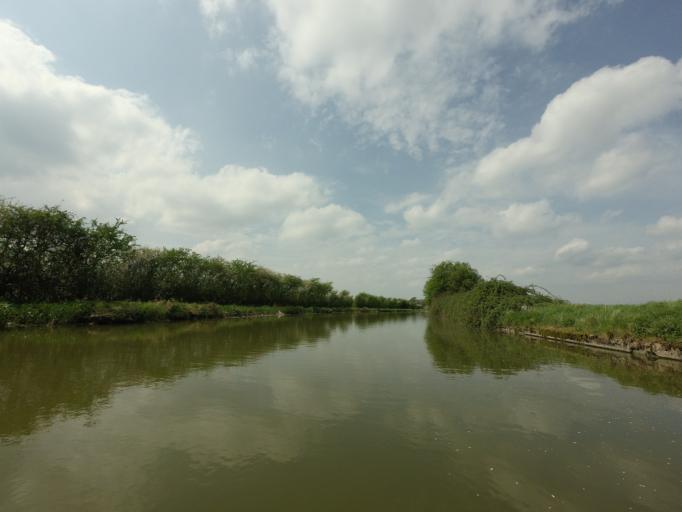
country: GB
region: England
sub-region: Central Bedfordshire
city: Leighton Buzzard
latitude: 51.8857
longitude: -0.6575
